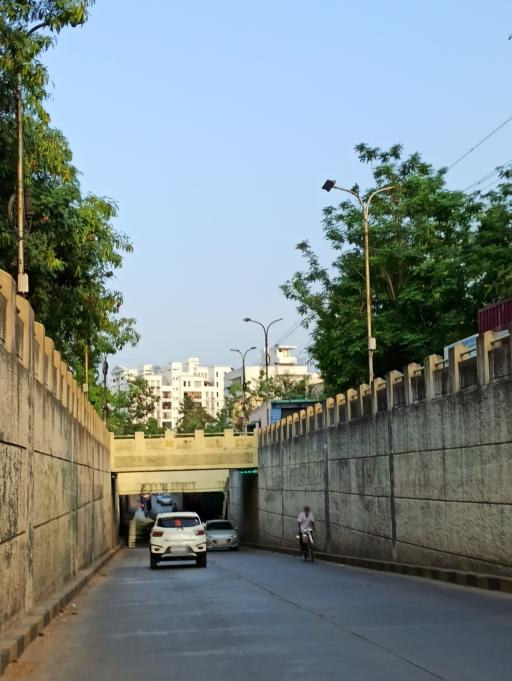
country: IN
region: Tamil Nadu
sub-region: Chennai
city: Chetput
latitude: 13.0701
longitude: 80.2328
